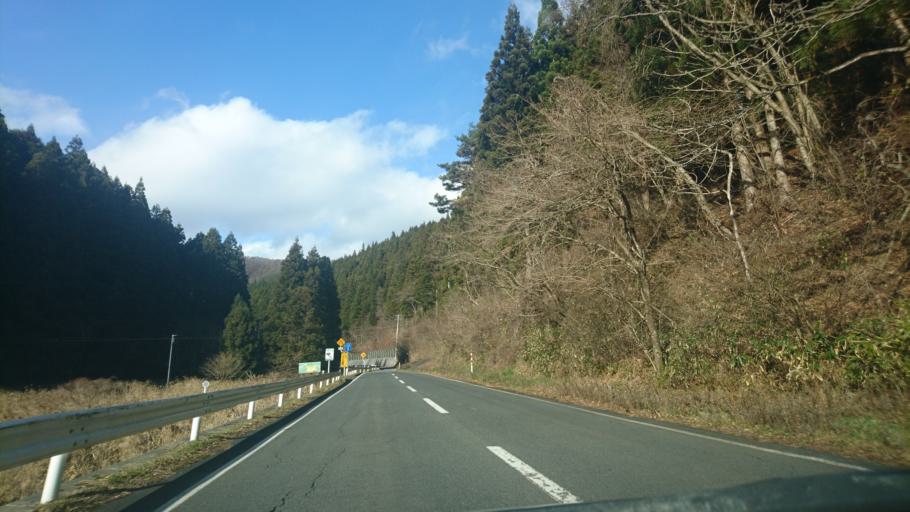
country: JP
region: Iwate
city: Mizusawa
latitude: 39.0949
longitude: 141.3865
